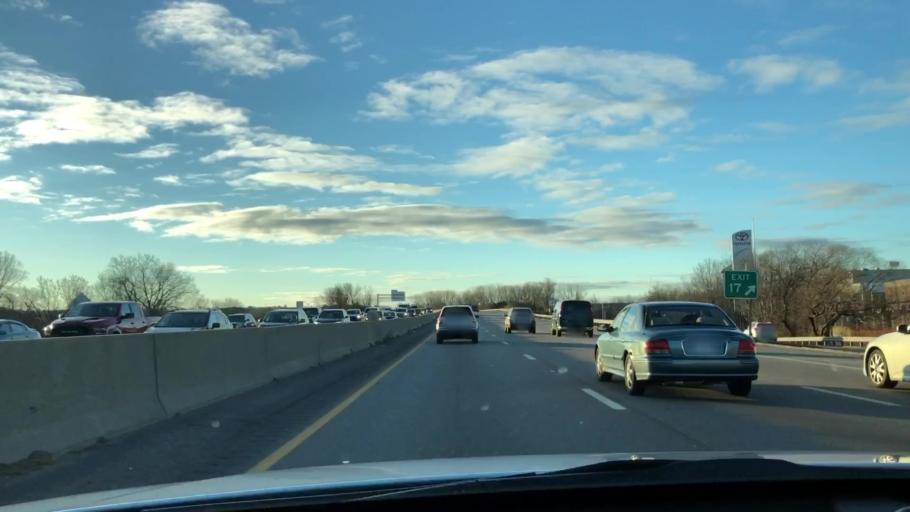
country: US
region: Massachusetts
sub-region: Norfolk County
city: Braintree
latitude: 42.2133
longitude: -70.9969
